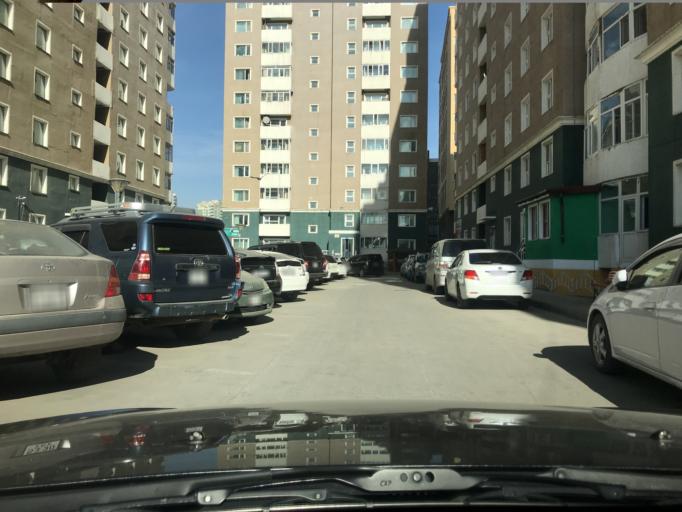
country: MN
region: Ulaanbaatar
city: Ulaanbaatar
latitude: 47.9114
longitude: 106.9473
